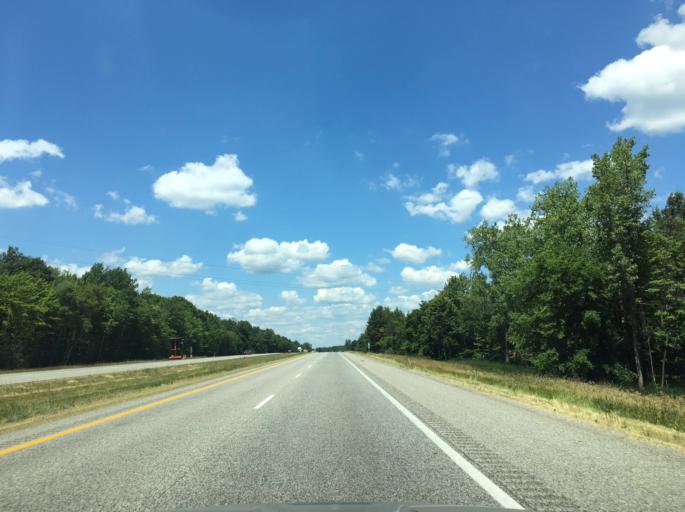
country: US
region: Michigan
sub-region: Midland County
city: Midland
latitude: 43.6484
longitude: -84.1959
